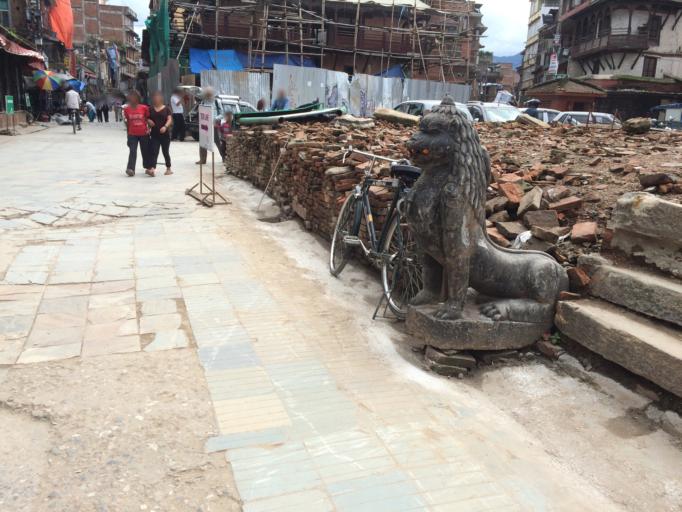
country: NP
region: Central Region
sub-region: Bagmati Zone
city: Kathmandu
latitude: 27.7040
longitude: 85.3060
